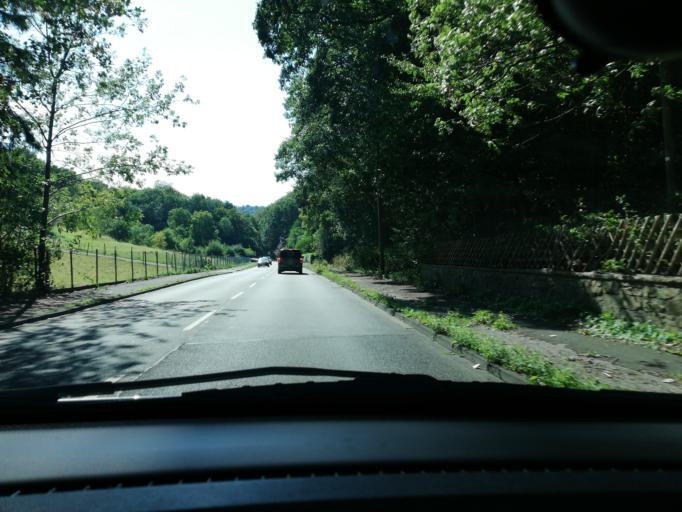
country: DE
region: North Rhine-Westphalia
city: Witten
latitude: 51.4249
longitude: 7.3601
